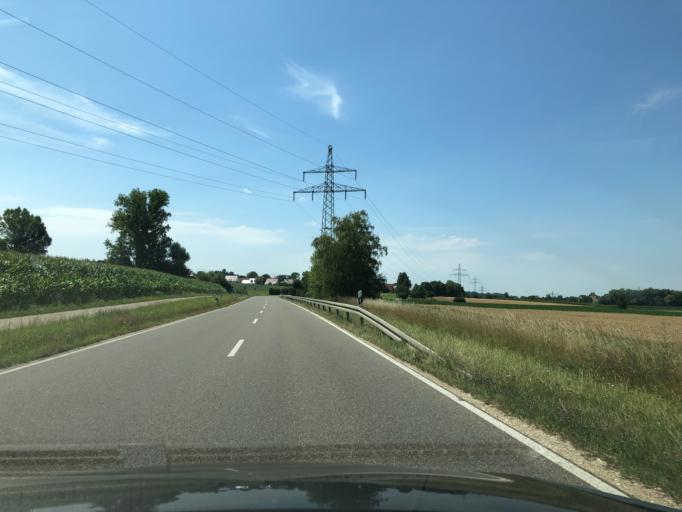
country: DE
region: Bavaria
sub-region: Swabia
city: Wertingen
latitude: 48.5689
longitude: 10.7042
